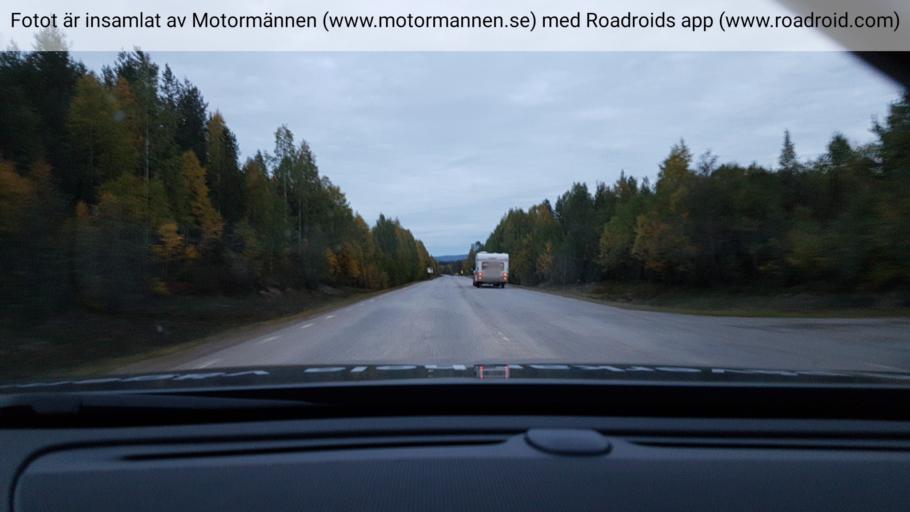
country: SE
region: Norrbotten
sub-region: Alvsbyns Kommun
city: AElvsbyn
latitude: 65.8420
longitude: 20.4988
